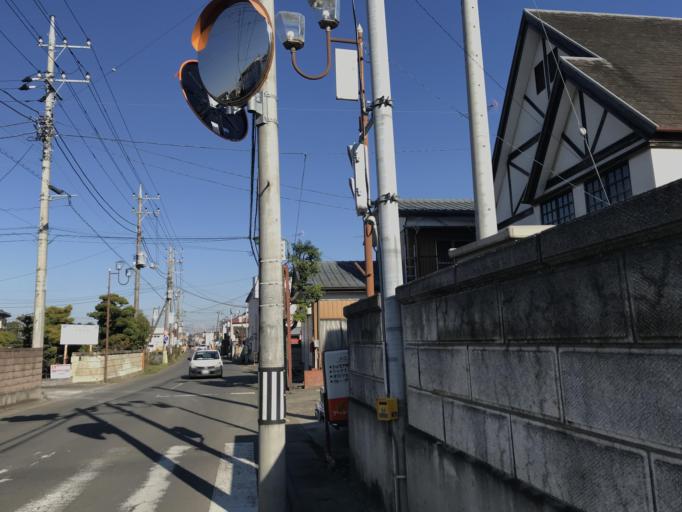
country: JP
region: Ibaraki
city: Yuki
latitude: 36.2976
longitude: 139.8683
